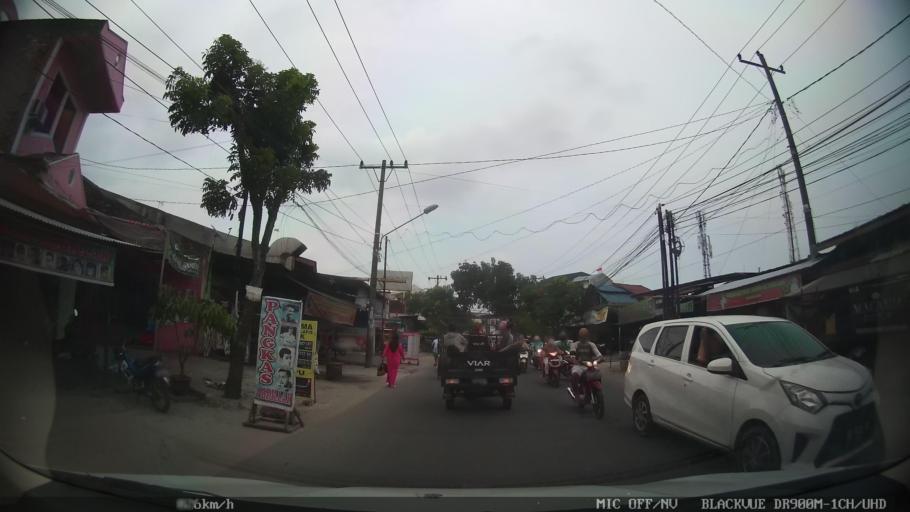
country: ID
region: North Sumatra
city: Medan
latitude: 3.5773
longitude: 98.7273
